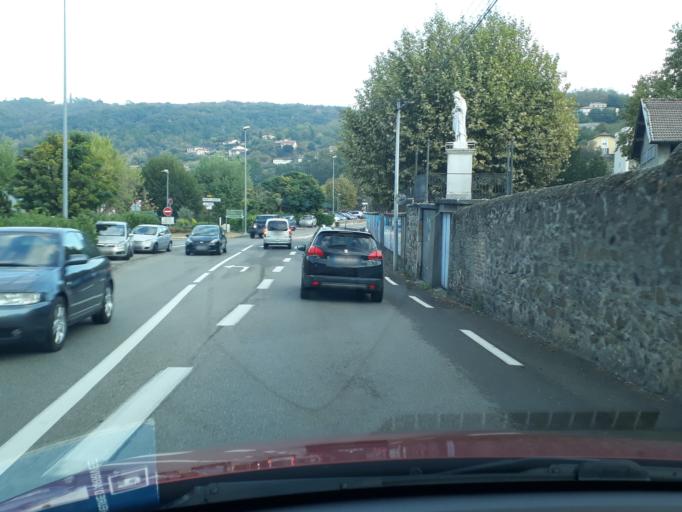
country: FR
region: Rhone-Alpes
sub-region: Departement de l'Isere
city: Les Roches-de-Condrieu
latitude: 45.4548
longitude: 4.7714
